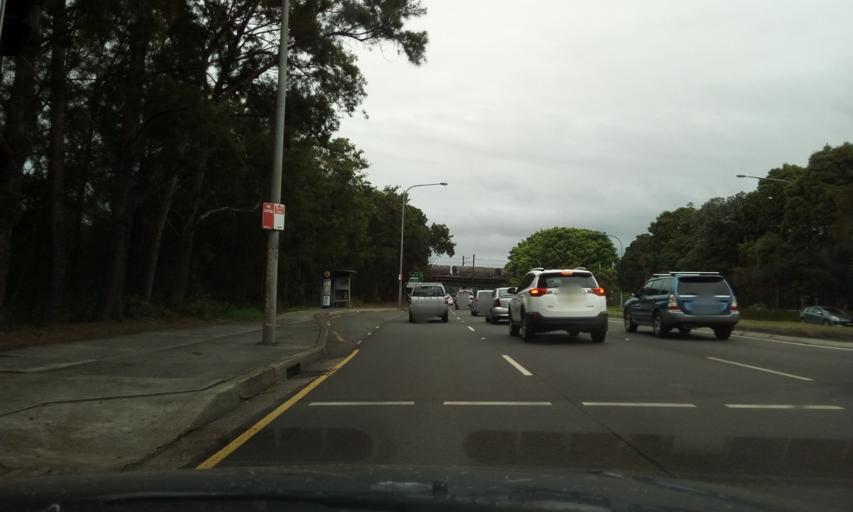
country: AU
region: New South Wales
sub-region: Wollongong
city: Coniston
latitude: -34.4412
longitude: 150.8889
